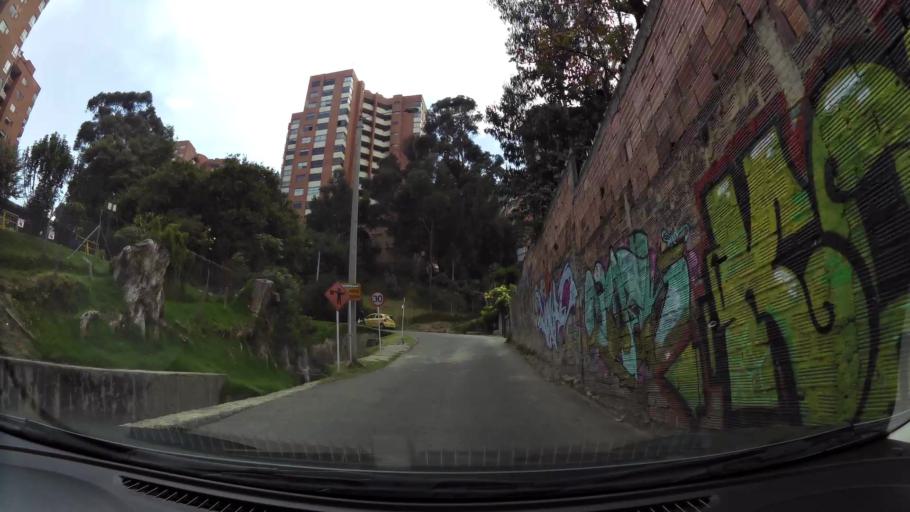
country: CO
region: Bogota D.C.
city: Barrio San Luis
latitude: 4.7020
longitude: -74.0282
